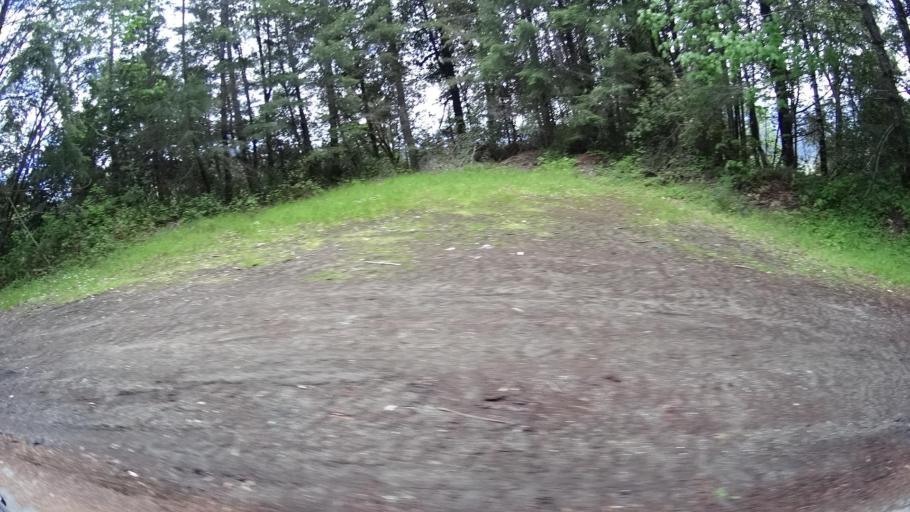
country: US
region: California
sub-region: Humboldt County
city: Blue Lake
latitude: 40.7594
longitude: -123.9076
